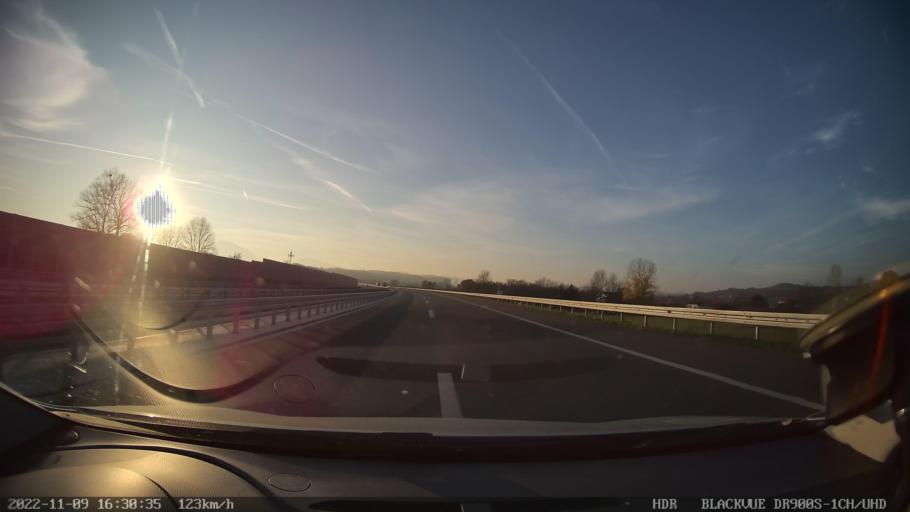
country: RS
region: Central Serbia
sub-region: Moravicki Okrug
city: Cacak
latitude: 43.9294
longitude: 20.3338
